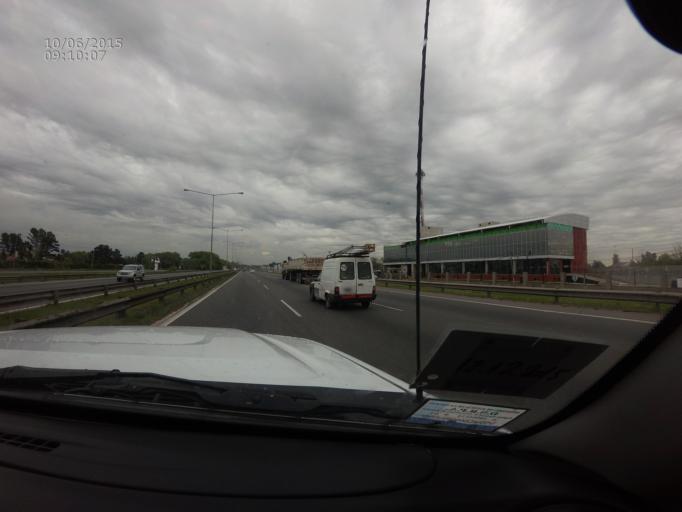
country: AR
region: Buenos Aires
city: Belen de Escobar
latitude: -34.3717
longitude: -58.7659
